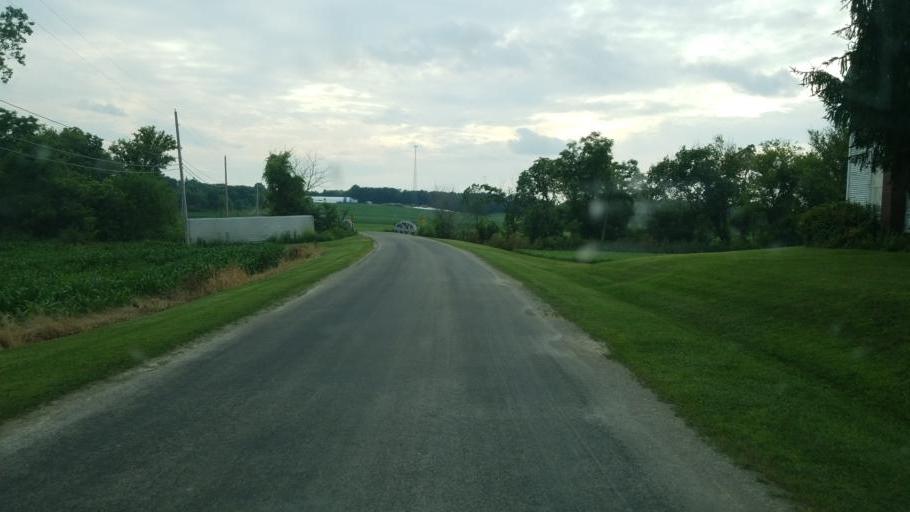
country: US
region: Ohio
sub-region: Wayne County
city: Shreve
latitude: 40.7805
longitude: -82.1036
